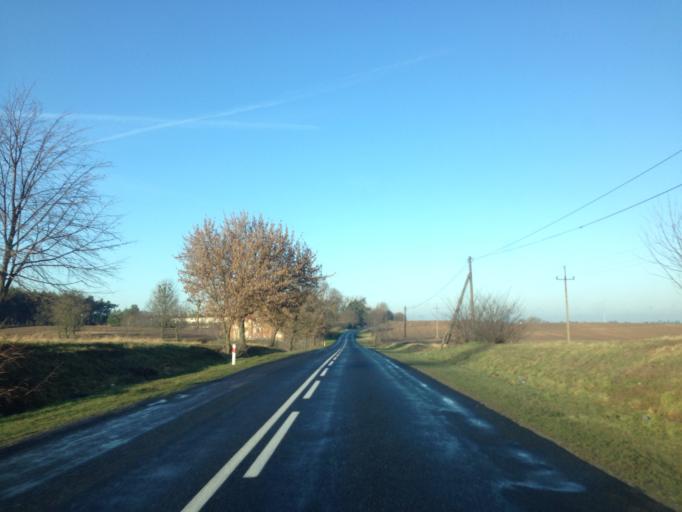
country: PL
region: Kujawsko-Pomorskie
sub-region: Powiat brodnicki
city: Bobrowo
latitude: 53.3304
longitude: 19.2346
